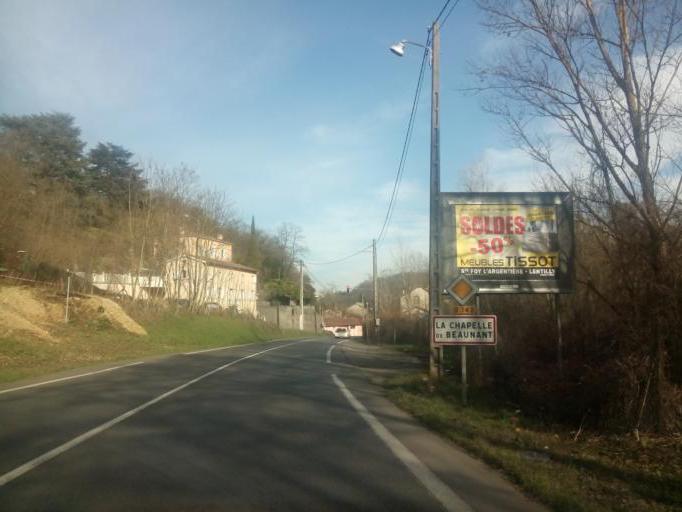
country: FR
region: Rhone-Alpes
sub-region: Departement du Rhone
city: Francheville
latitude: 45.7158
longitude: 4.7761
